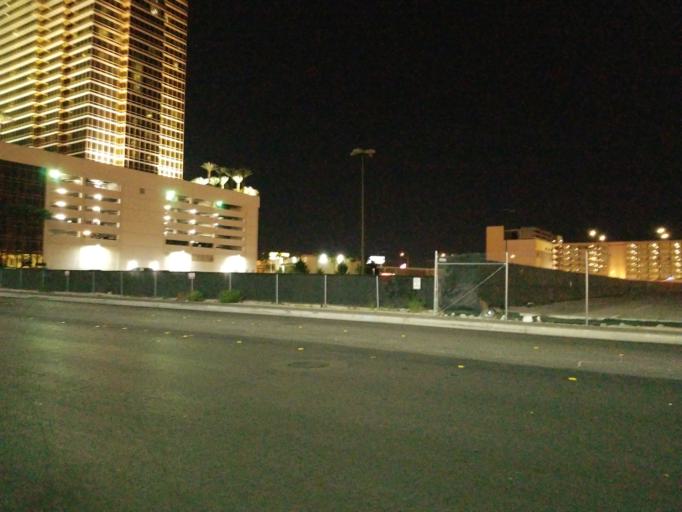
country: US
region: Nevada
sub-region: Clark County
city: Paradise
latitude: 36.1288
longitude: -115.1708
